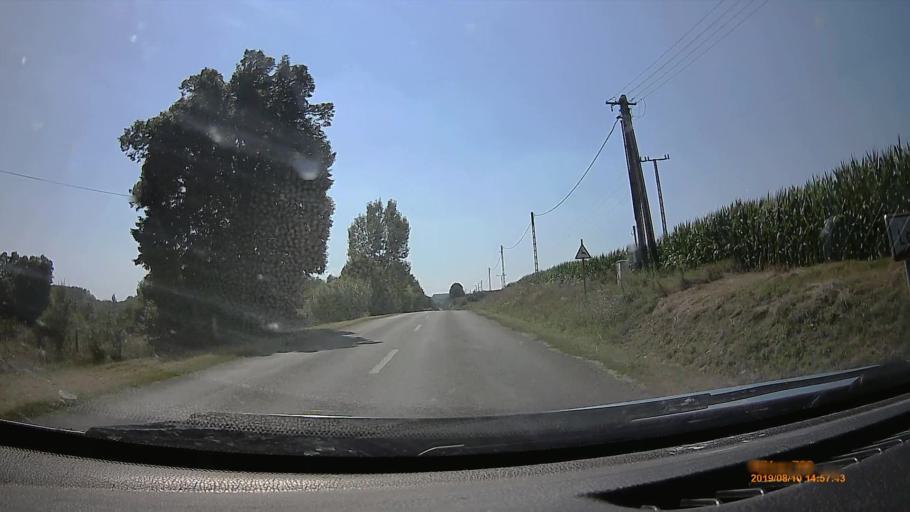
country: HU
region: Somogy
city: Lengyeltoti
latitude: 46.6594
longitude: 17.6219
